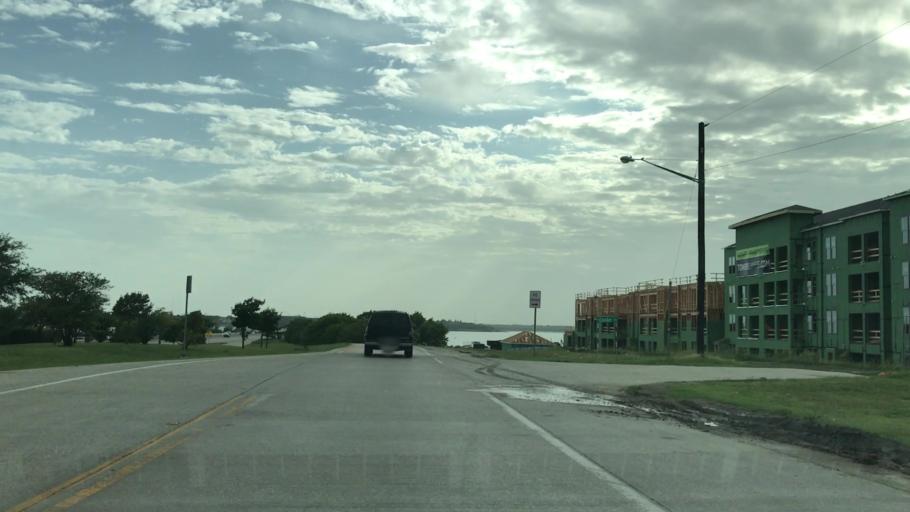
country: US
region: Texas
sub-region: Dallas County
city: Rowlett
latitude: 32.8761
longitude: -96.5205
